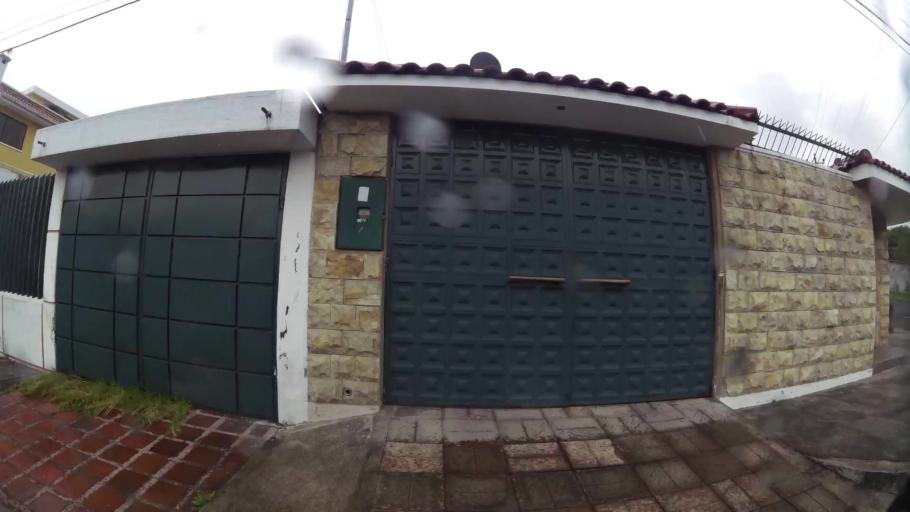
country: EC
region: Pichincha
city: Sangolqui
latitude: -0.2871
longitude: -78.4660
